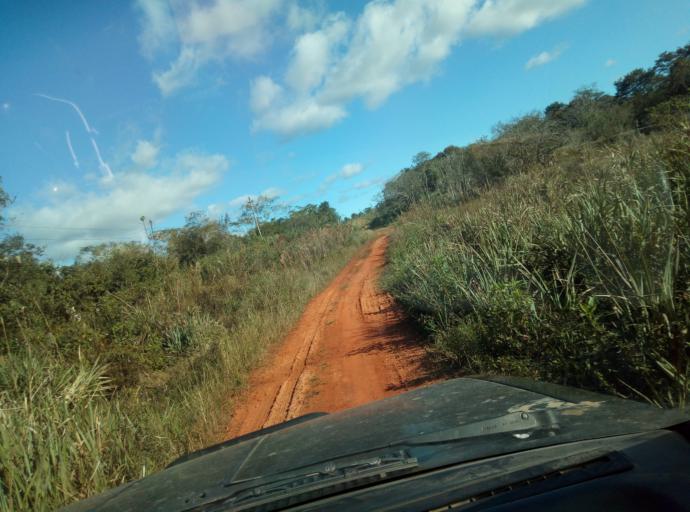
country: PY
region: Caaguazu
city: Carayao
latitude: -25.1715
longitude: -56.2732
